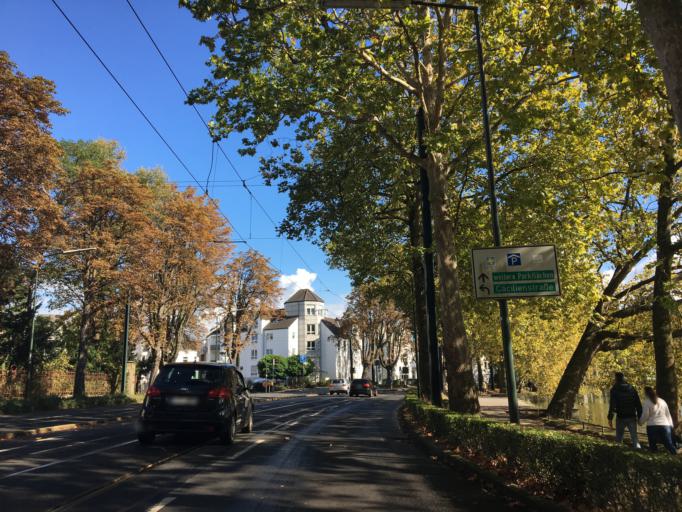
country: DE
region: North Rhine-Westphalia
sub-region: Regierungsbezirk Dusseldorf
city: Hilden
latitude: 51.1631
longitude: 6.8698
